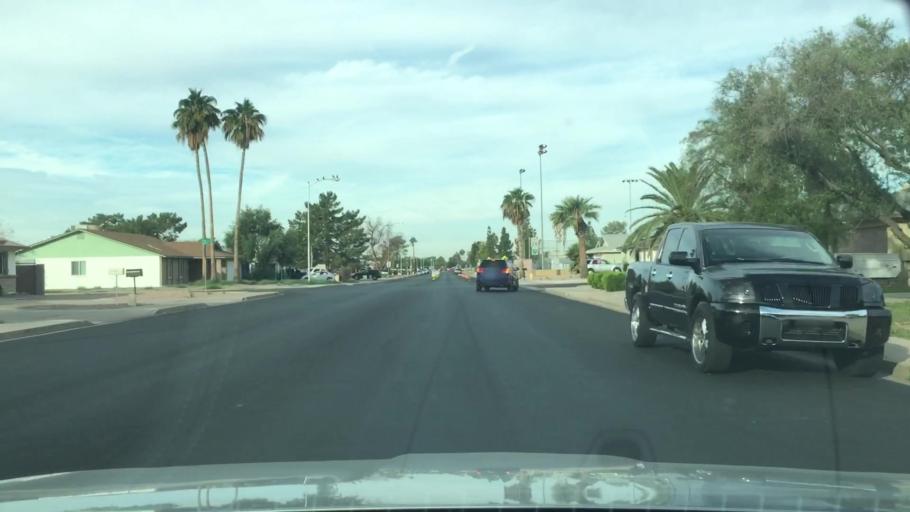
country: US
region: Arizona
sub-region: Maricopa County
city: Gilbert
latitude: 33.4010
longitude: -111.7570
